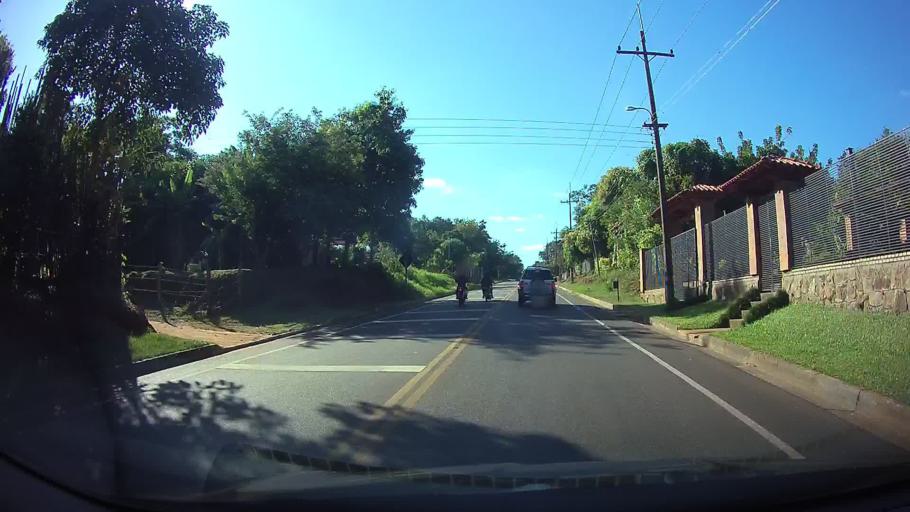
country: PY
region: Cordillera
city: Atyra
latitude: -25.3135
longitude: -57.1466
